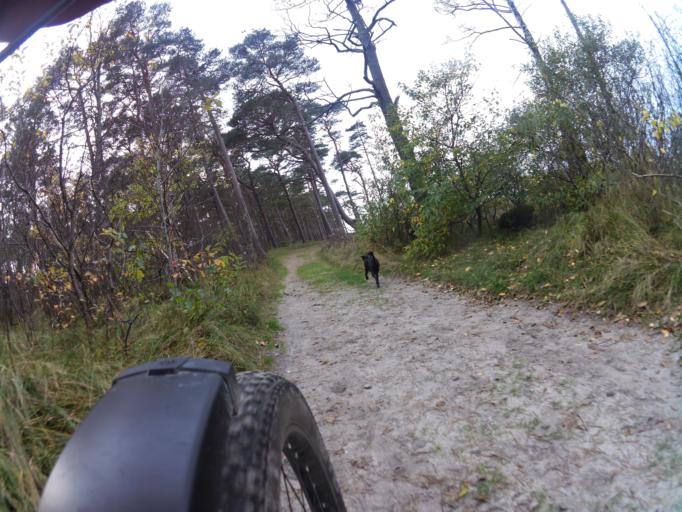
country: PL
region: Pomeranian Voivodeship
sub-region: Powiat wejherowski
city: Choczewo
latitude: 54.8091
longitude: 17.8229
